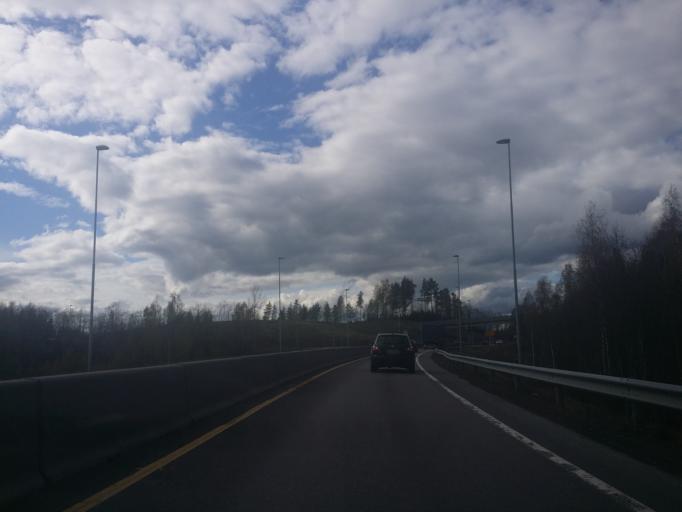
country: NO
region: Buskerud
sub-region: Ringerike
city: Honefoss
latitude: 60.1499
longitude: 10.2219
